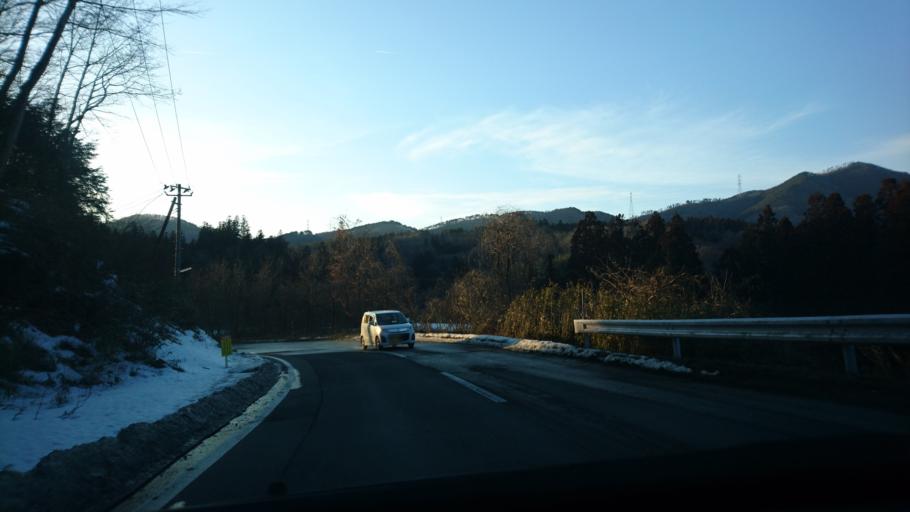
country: JP
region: Iwate
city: Mizusawa
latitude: 39.0462
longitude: 141.3343
